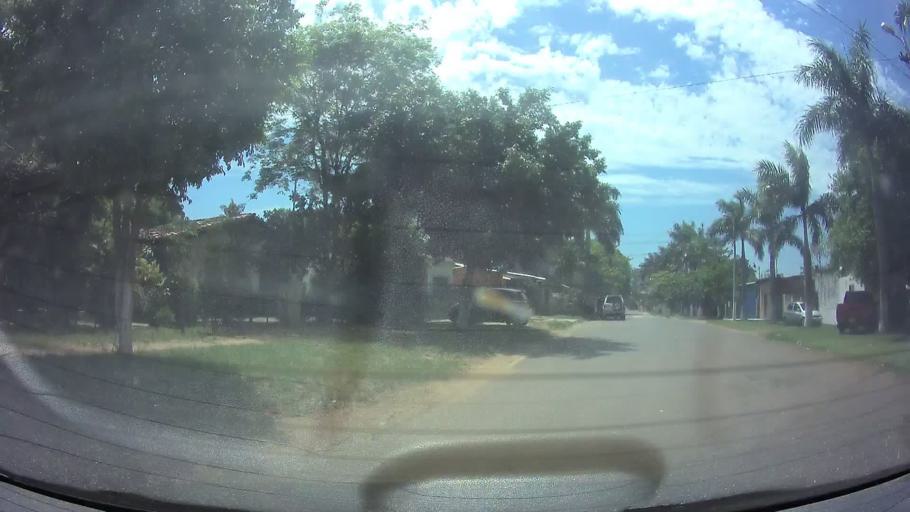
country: PY
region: Central
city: Limpio
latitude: -25.1720
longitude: -57.4775
